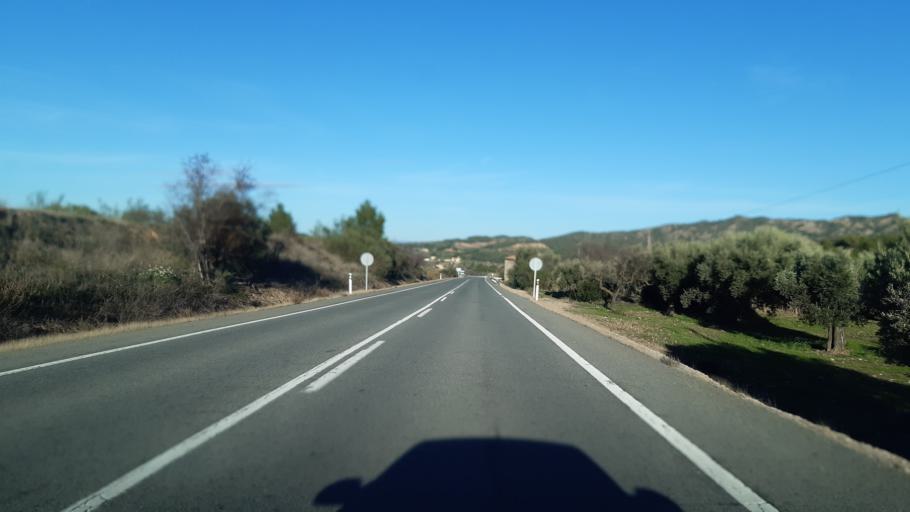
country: ES
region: Catalonia
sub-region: Provincia de Tarragona
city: la Fatarella
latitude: 41.1018
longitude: 0.5235
